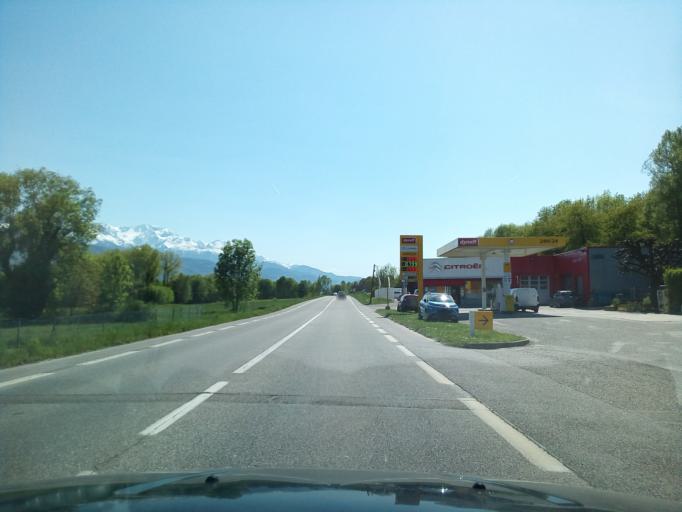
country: FR
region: Rhone-Alpes
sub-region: Departement de l'Isere
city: Le Touvet
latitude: 45.3497
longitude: 5.9464
